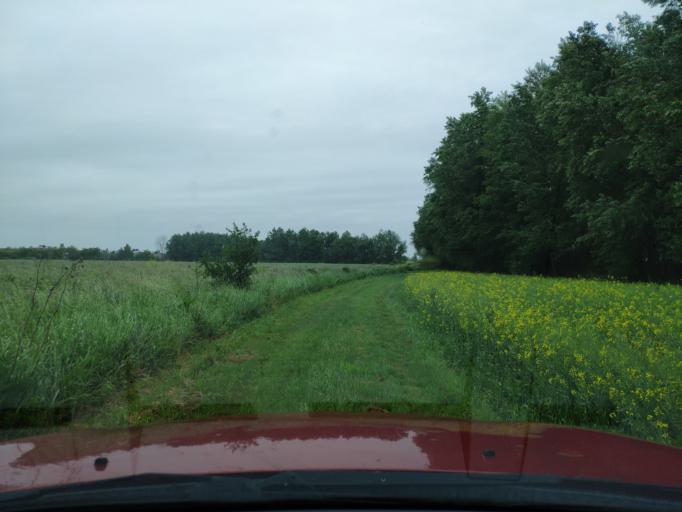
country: SK
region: Kosicky
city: Cierna nad Tisou
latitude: 48.4175
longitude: 22.0419
